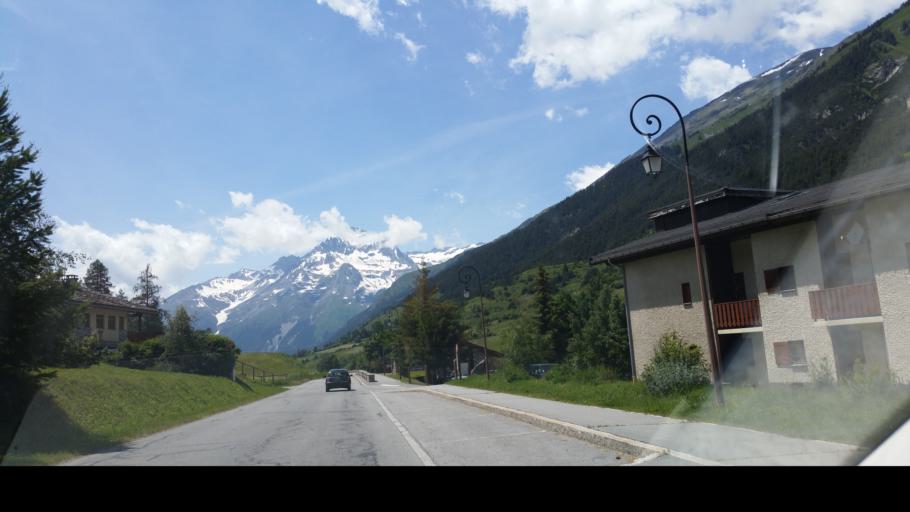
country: IT
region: Piedmont
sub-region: Provincia di Torino
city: Moncenisio
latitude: 45.2904
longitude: 6.9099
